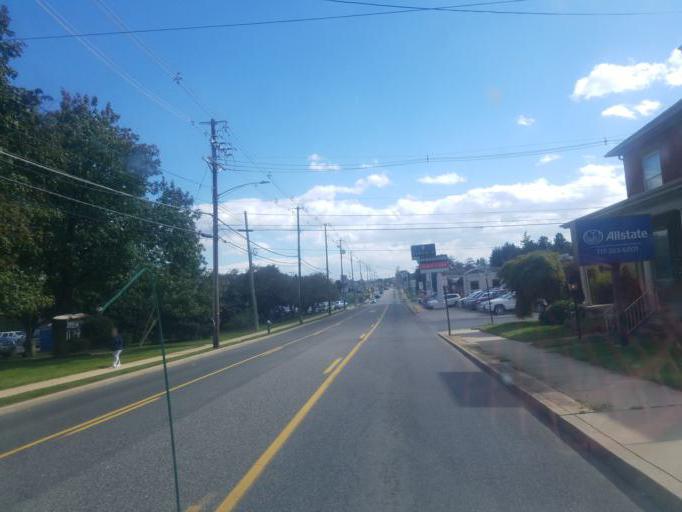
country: US
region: Pennsylvania
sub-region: Franklin County
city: Chambersburg
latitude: 39.9328
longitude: -77.6469
